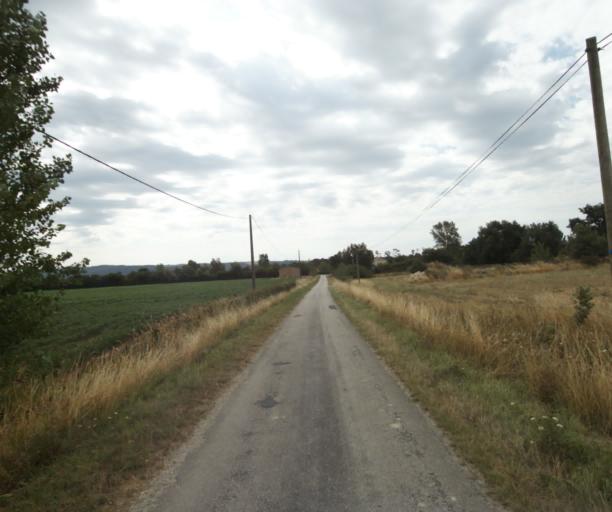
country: FR
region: Midi-Pyrenees
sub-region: Departement de la Haute-Garonne
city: Saint-Felix-Lauragais
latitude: 43.4341
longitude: 1.9384
